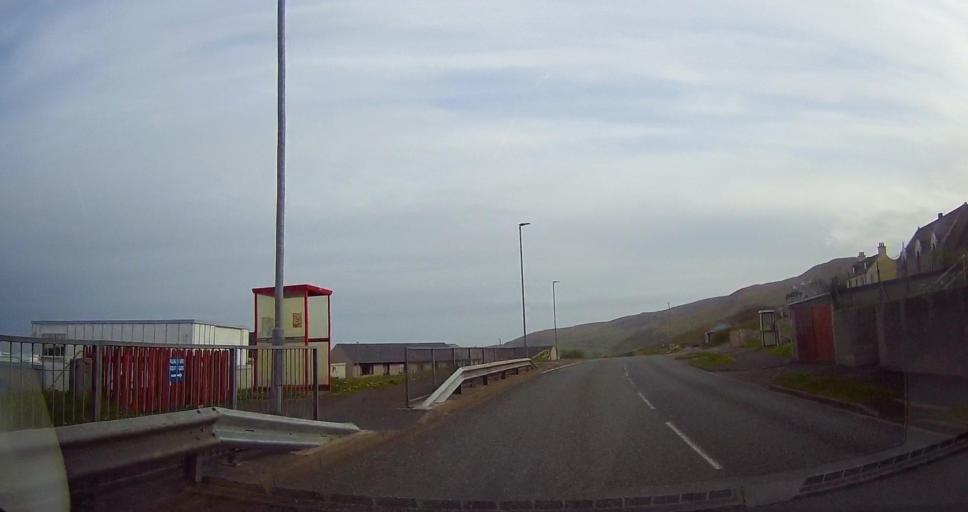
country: GB
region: Scotland
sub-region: Shetland Islands
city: Sandwick
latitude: 60.0464
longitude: -1.2278
